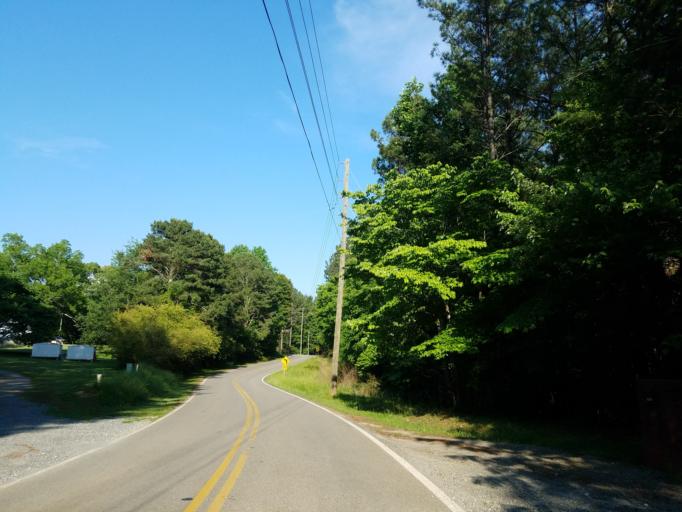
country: US
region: Georgia
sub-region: Pickens County
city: Nelson
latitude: 34.3715
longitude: -84.3291
